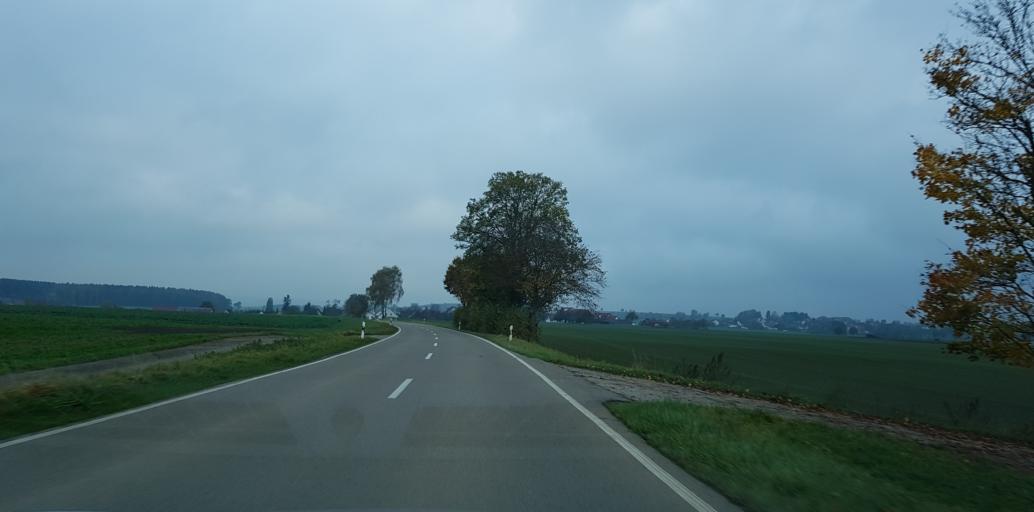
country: DE
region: Baden-Wuerttemberg
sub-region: Tuebingen Region
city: Opfingen
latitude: 48.3101
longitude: 9.7952
